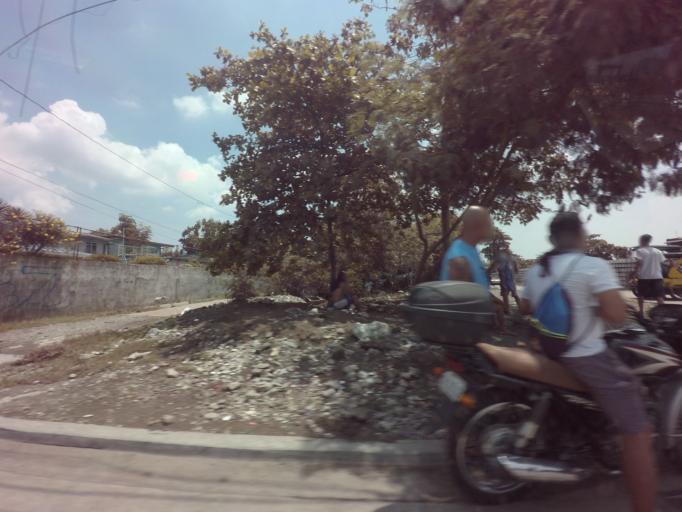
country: PH
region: Calabarzon
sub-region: Province of Laguna
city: San Pedro
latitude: 14.3906
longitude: 121.0474
